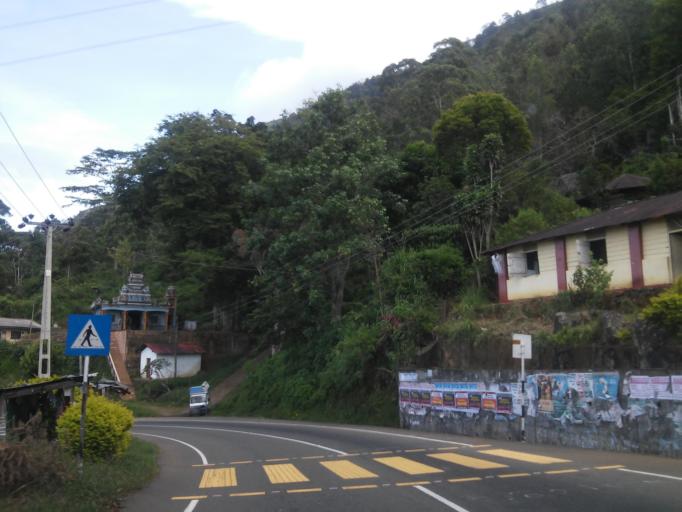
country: LK
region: Uva
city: Haputale
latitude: 6.7630
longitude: 80.9255
